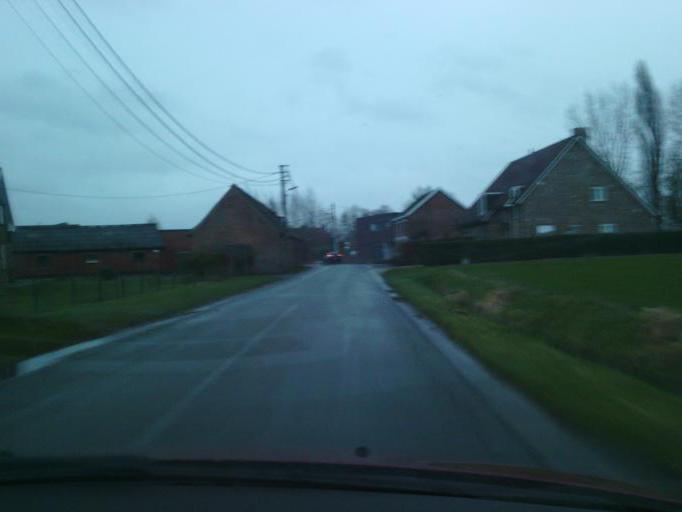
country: BE
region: Flanders
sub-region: Provincie Oost-Vlaanderen
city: Lokeren
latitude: 51.0704
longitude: 3.9976
